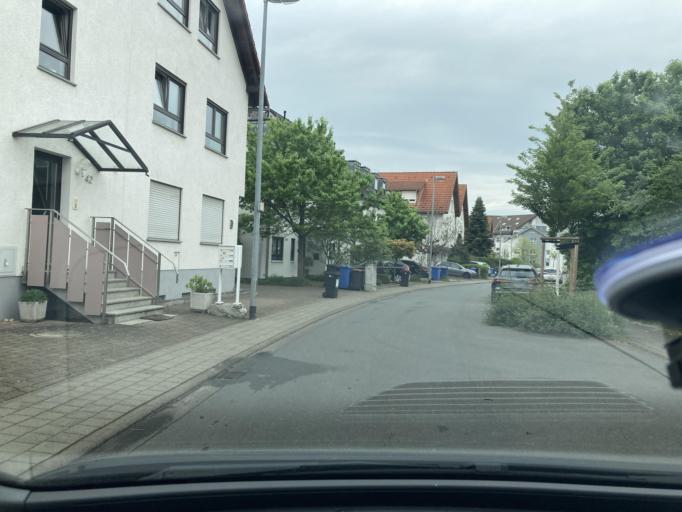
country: DE
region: Hesse
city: Langen
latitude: 49.9932
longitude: 8.6747
